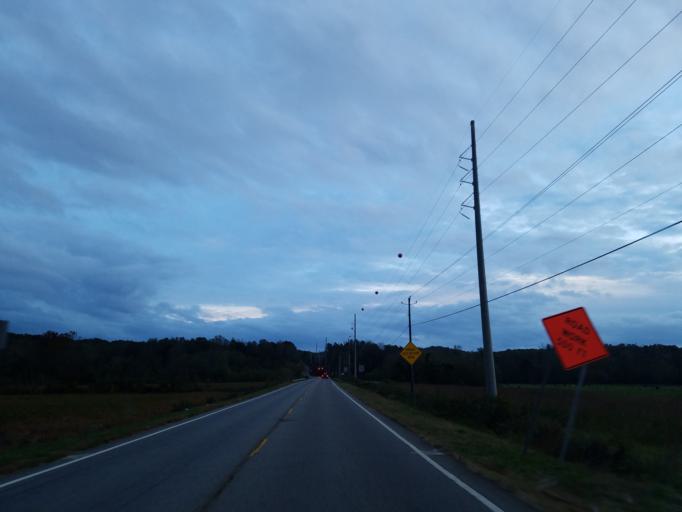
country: US
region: Georgia
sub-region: Dawson County
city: Dawsonville
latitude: 34.3621
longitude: -84.1133
